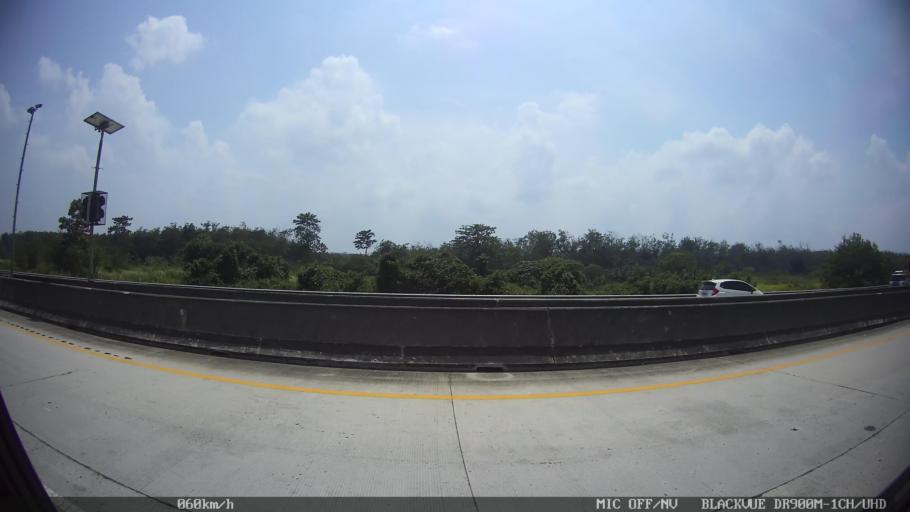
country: ID
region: Lampung
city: Kedaton
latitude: -5.3764
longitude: 105.3294
